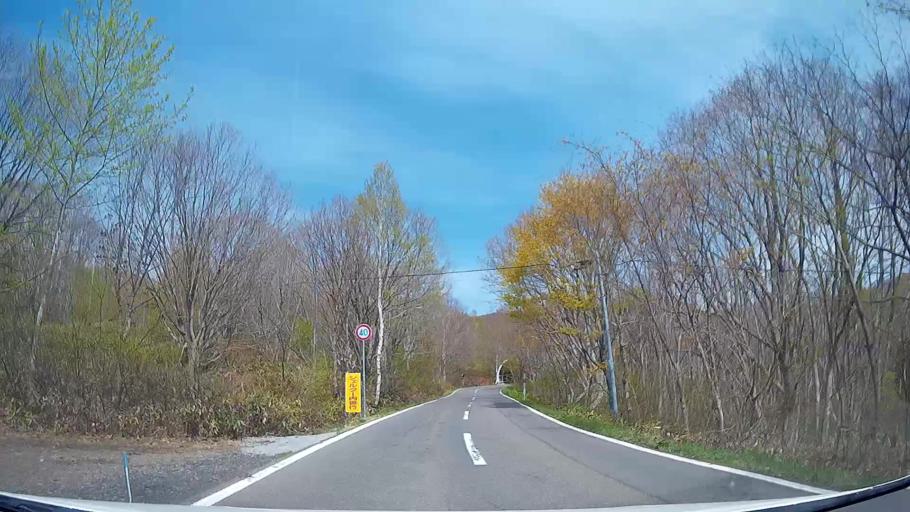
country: JP
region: Iwate
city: Shizukuishi
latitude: 39.9281
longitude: 140.9591
